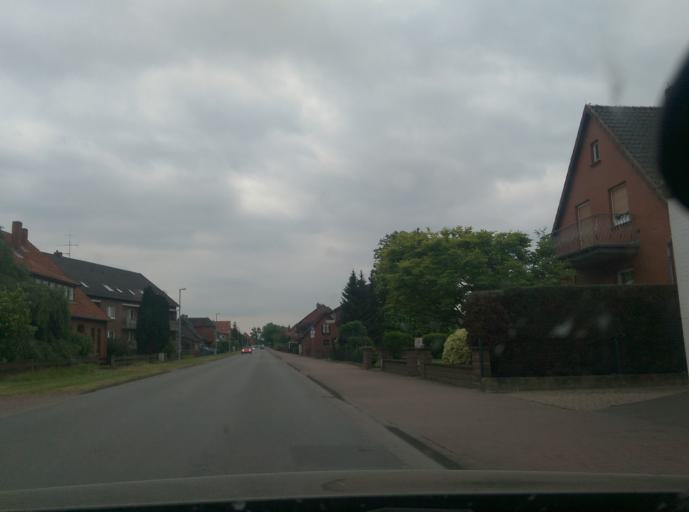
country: DE
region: Lower Saxony
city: Garbsen-Mitte
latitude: 52.4624
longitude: 9.6032
